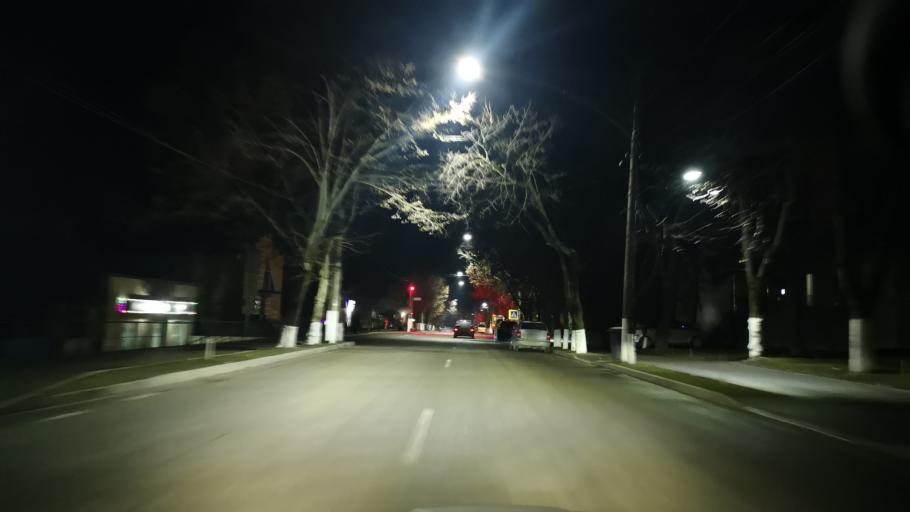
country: MD
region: Orhei
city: Orhei
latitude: 47.3878
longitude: 28.8242
